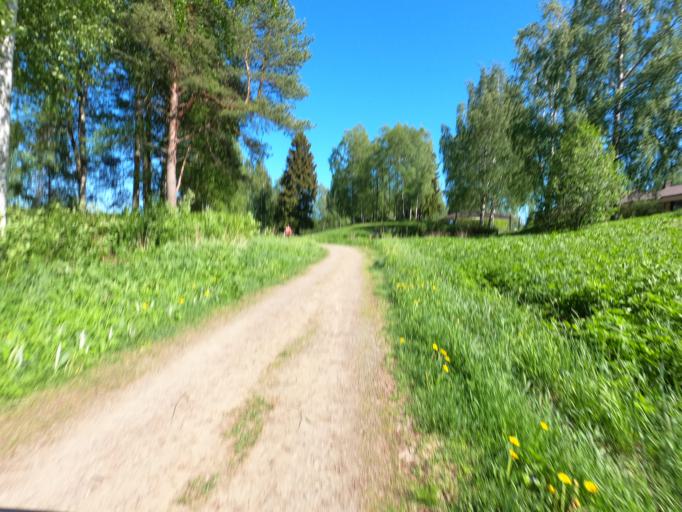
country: FI
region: North Karelia
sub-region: Joensuu
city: Joensuu
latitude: 62.6076
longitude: 29.8039
